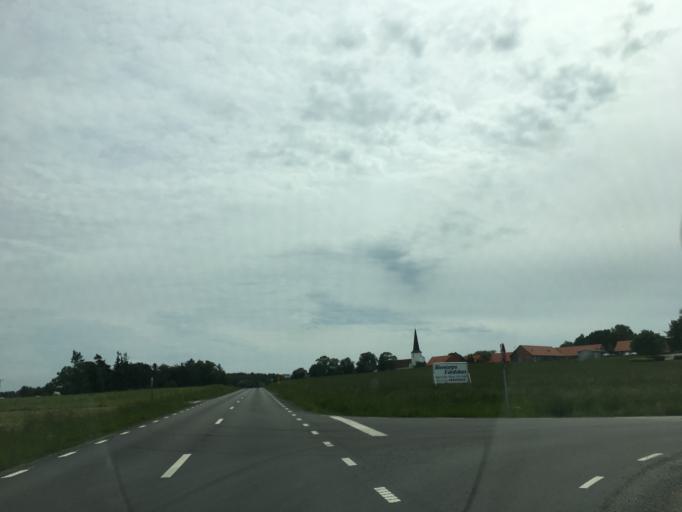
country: SE
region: Skane
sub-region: Sjobo Kommun
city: Blentarp
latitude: 55.5851
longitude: 13.6055
